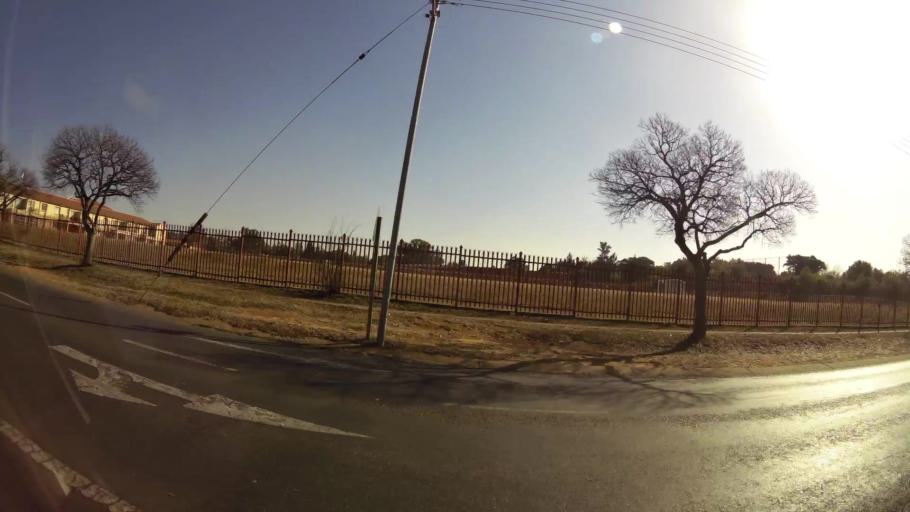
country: ZA
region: Gauteng
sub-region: City of Tshwane Metropolitan Municipality
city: Pretoria
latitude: -25.7290
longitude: 28.2459
